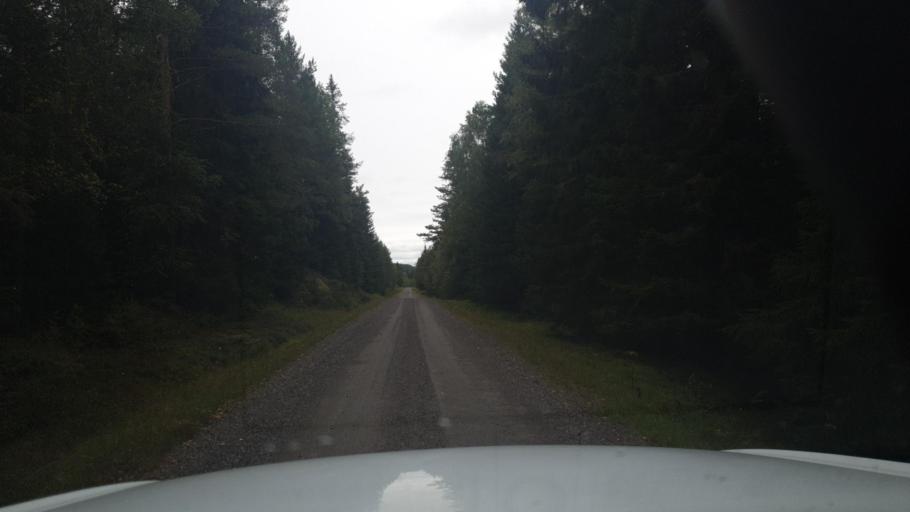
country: SE
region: Vaermland
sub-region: Eda Kommun
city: Charlottenberg
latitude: 60.1213
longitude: 12.5999
